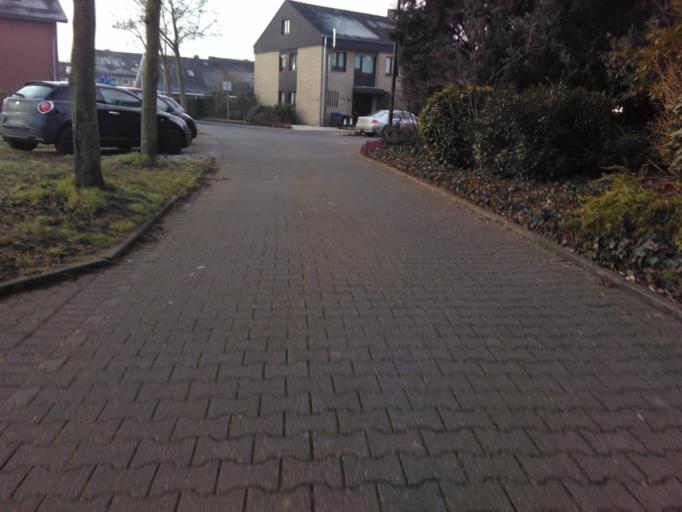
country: DE
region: North Rhine-Westphalia
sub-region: Regierungsbezirk Detmold
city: Verl
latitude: 51.8849
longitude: 8.4927
